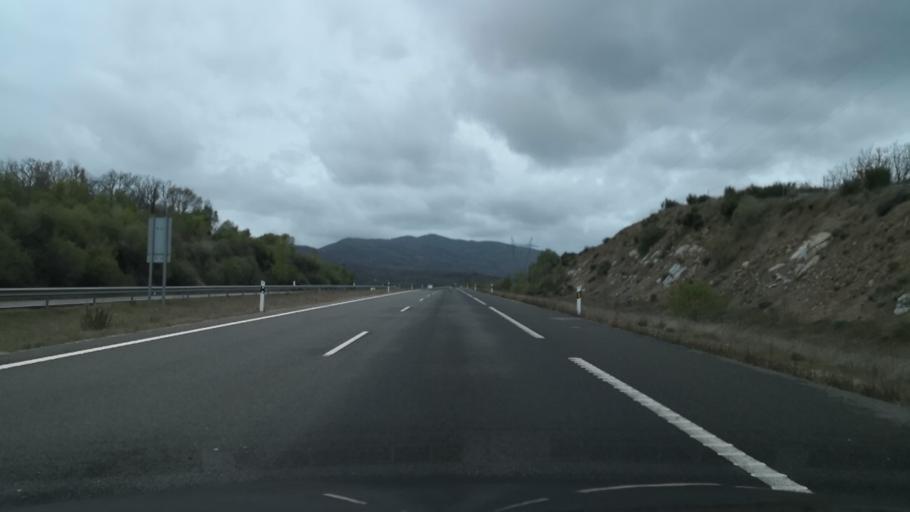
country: ES
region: Castille and Leon
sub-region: Provincia de Salamanca
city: Cantagallo
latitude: 40.3666
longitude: -5.8320
